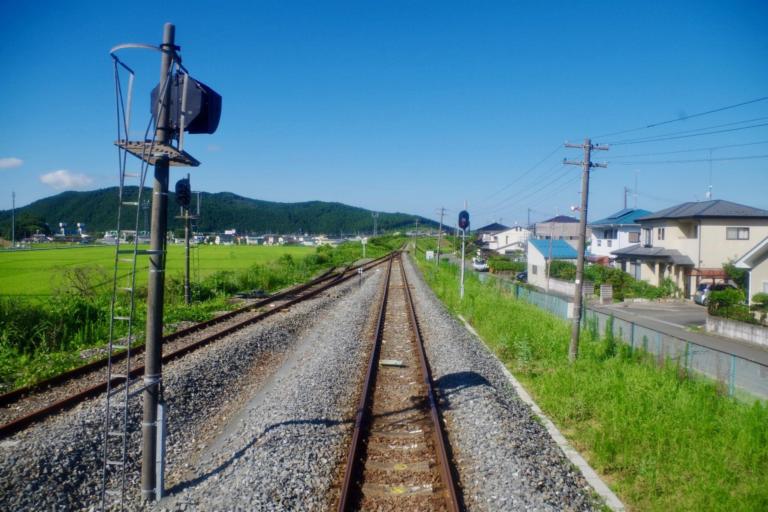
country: JP
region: Miyagi
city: Wakuya
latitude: 38.6112
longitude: 141.3050
